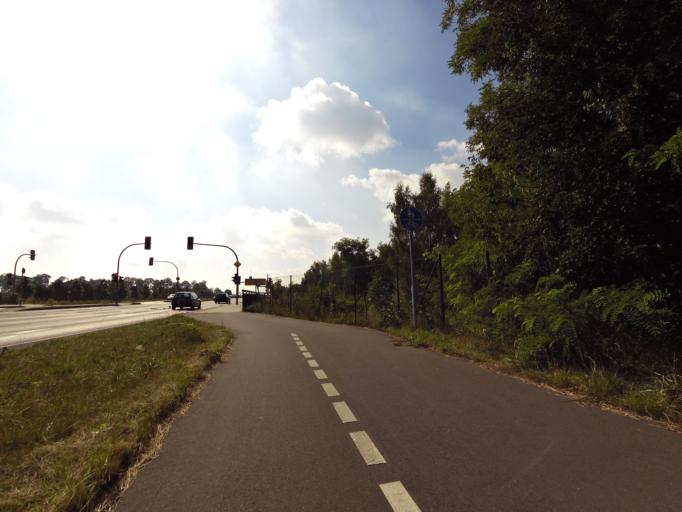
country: DE
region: Berlin
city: Lichtenrade
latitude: 52.3758
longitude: 13.4180
